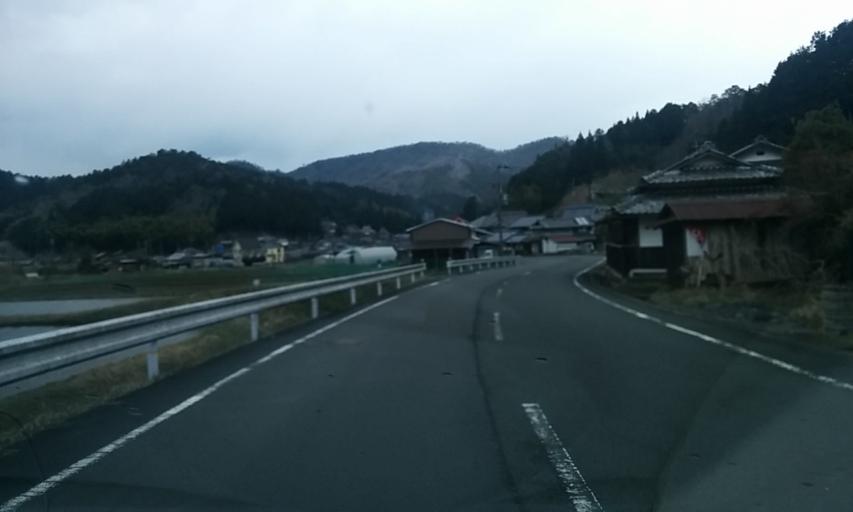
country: JP
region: Hyogo
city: Sasayama
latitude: 35.1241
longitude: 135.4155
